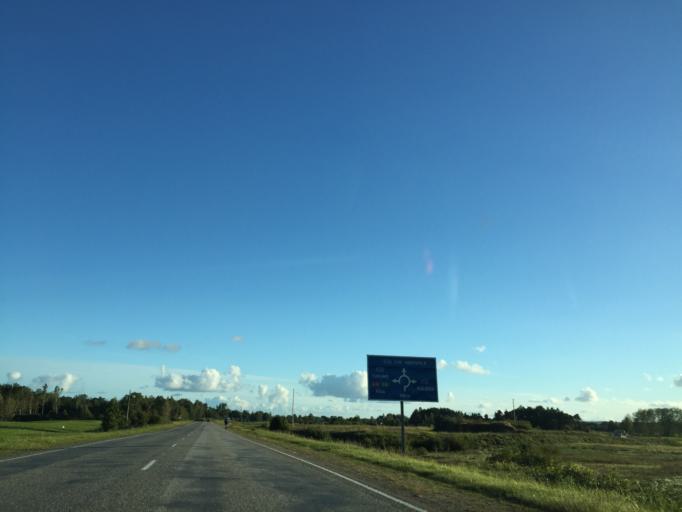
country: LV
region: Kuldigas Rajons
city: Kuldiga
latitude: 56.9762
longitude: 22.0160
